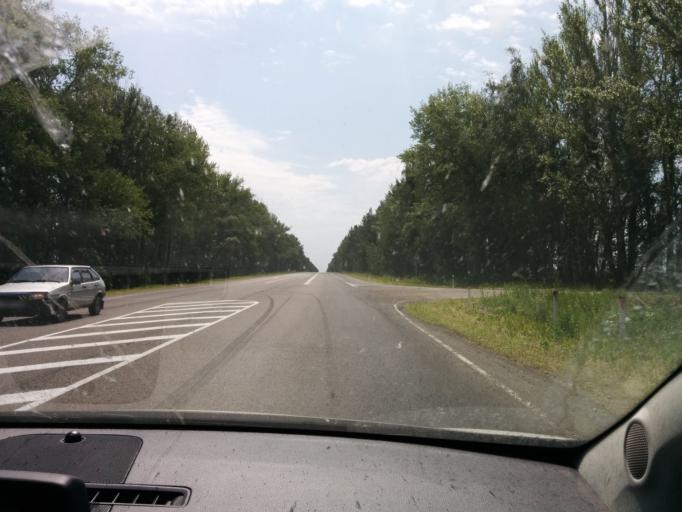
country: RU
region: Tambov
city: Morshansk
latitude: 53.5307
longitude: 41.7955
